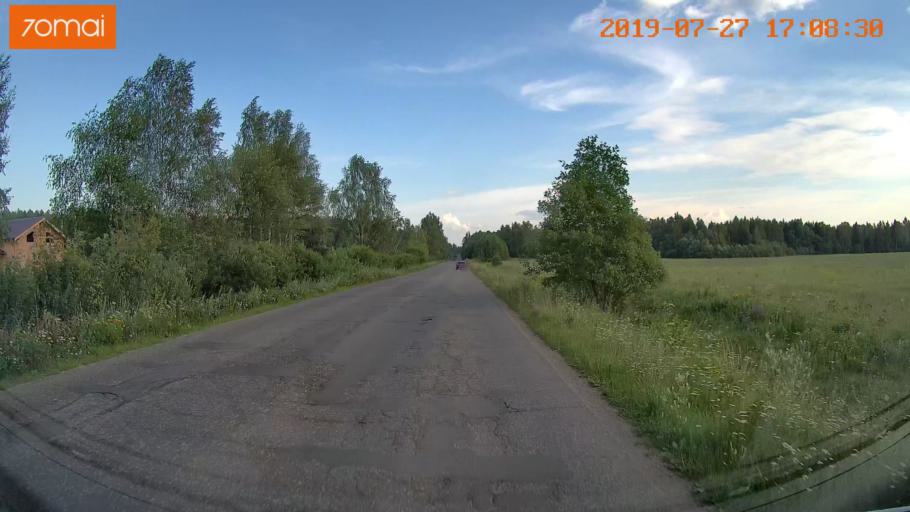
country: RU
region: Ivanovo
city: Novo-Talitsy
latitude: 57.0820
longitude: 40.8383
